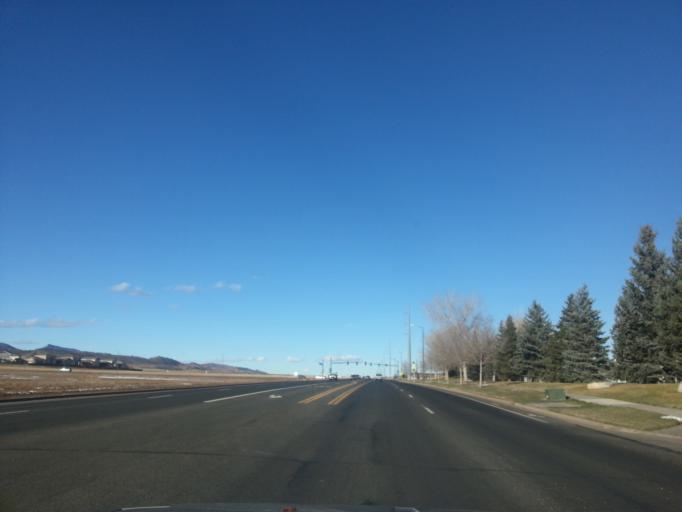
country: US
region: Colorado
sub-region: Larimer County
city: Loveland
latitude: 40.4342
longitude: -105.1155
